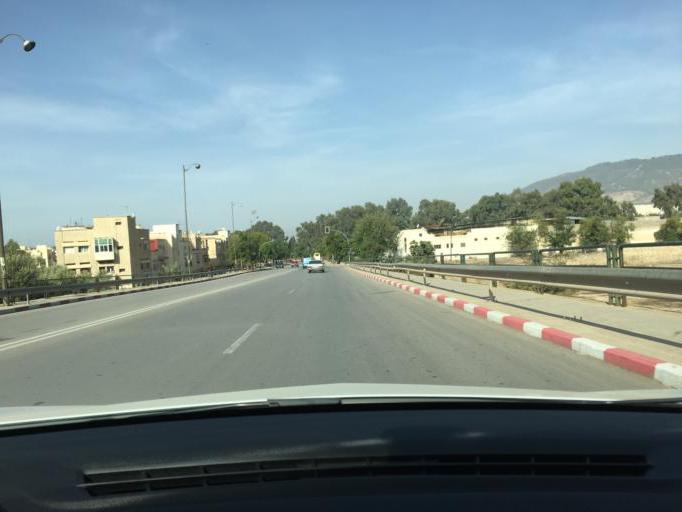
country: MA
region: Fes-Boulemane
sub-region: Fes
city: Fes
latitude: 34.0394
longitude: -5.0259
